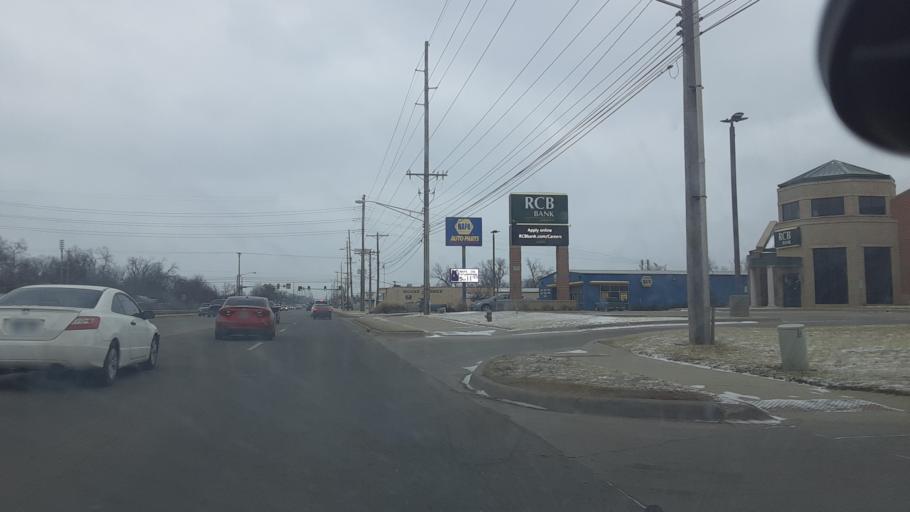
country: US
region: Oklahoma
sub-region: Payne County
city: Stillwater
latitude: 36.1172
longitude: -97.0513
